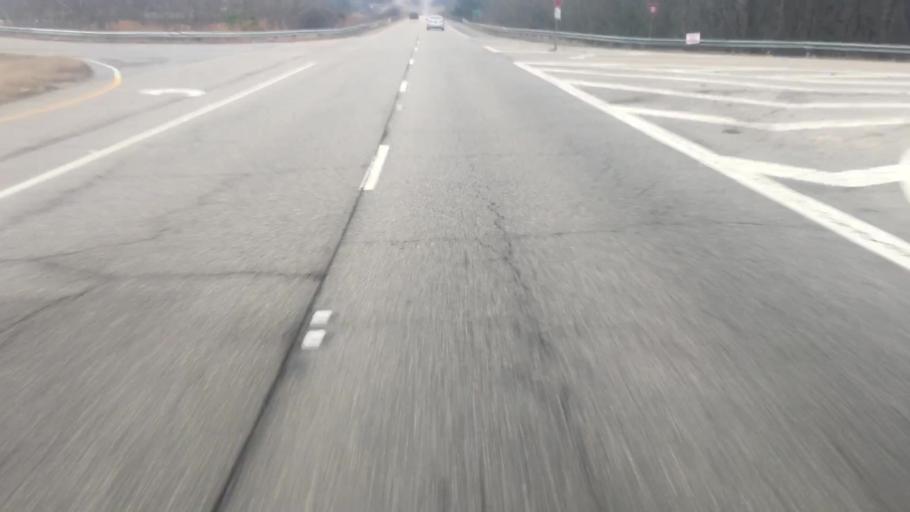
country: US
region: Alabama
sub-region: Walker County
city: Cordova
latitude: 33.8071
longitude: -87.1435
